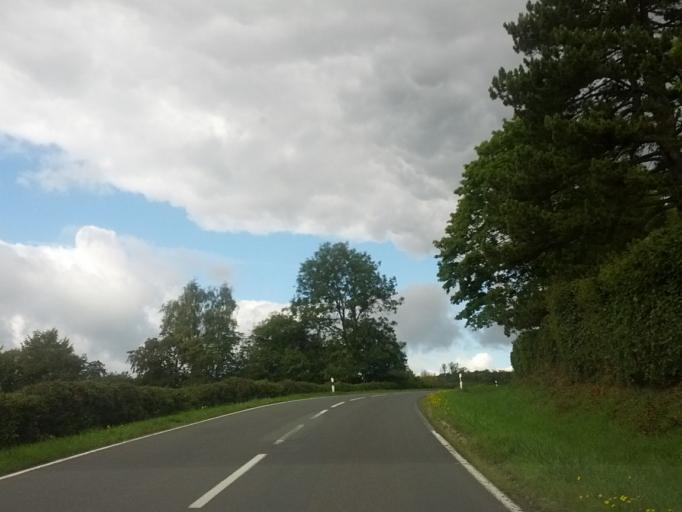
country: DE
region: Hesse
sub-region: Regierungsbezirk Kassel
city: Weissenborn
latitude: 51.0562
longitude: 10.1161
